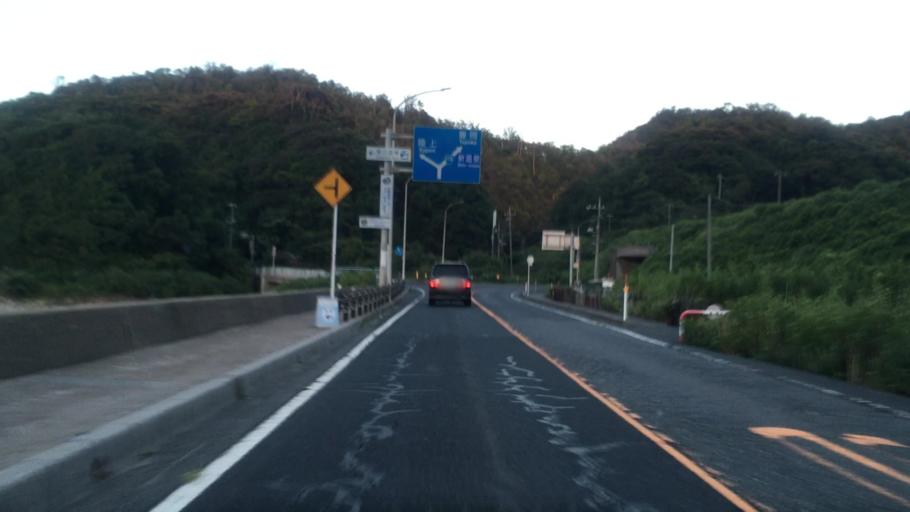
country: JP
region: Tottori
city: Tottori
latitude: 35.6001
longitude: 134.3502
